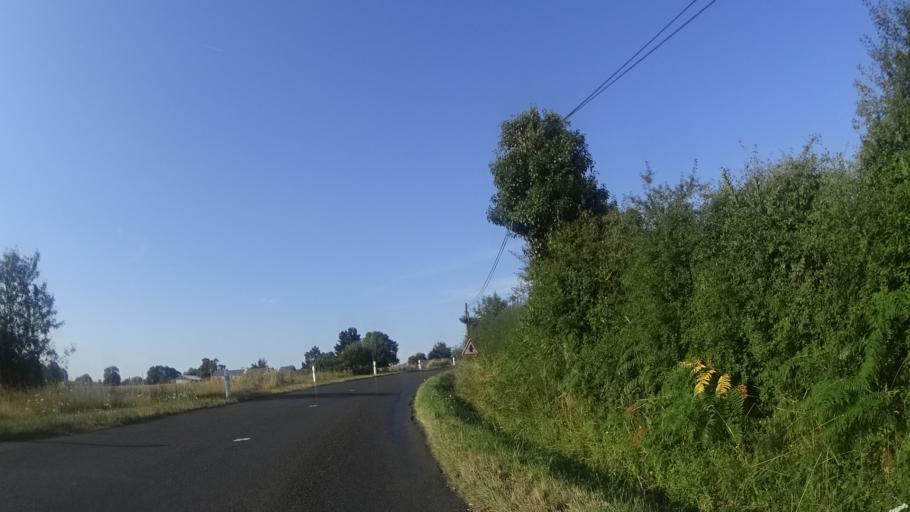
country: FR
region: Pays de la Loire
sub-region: Departement de la Loire-Atlantique
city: Riaille
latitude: 47.5016
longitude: -1.3078
